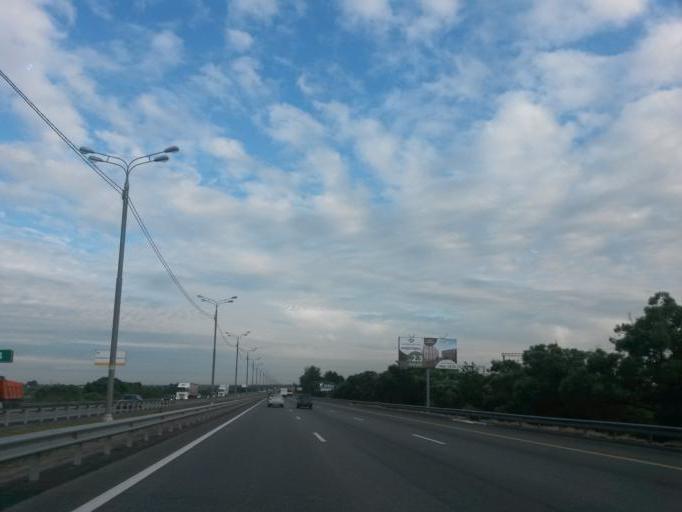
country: RU
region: Moskovskaya
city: Yam
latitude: 55.5117
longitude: 37.7154
